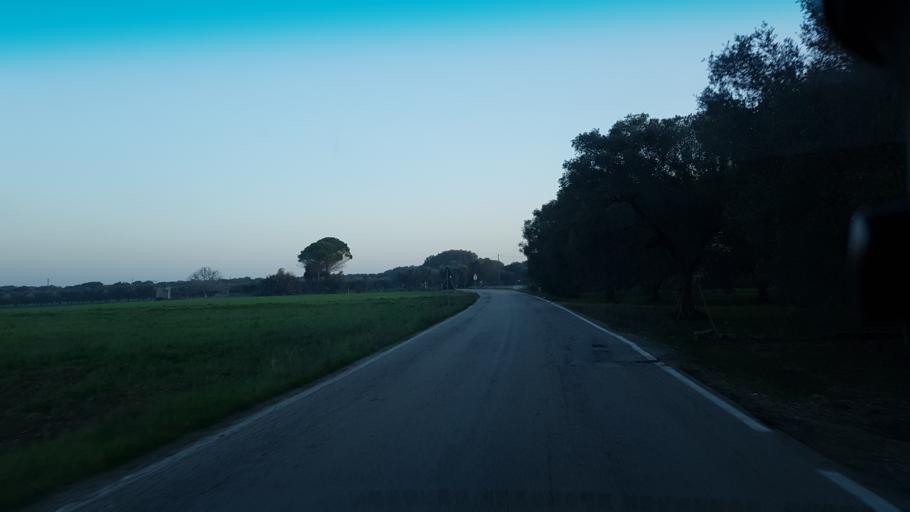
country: IT
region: Apulia
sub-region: Provincia di Brindisi
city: Mesagne
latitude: 40.6144
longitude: 17.7868
